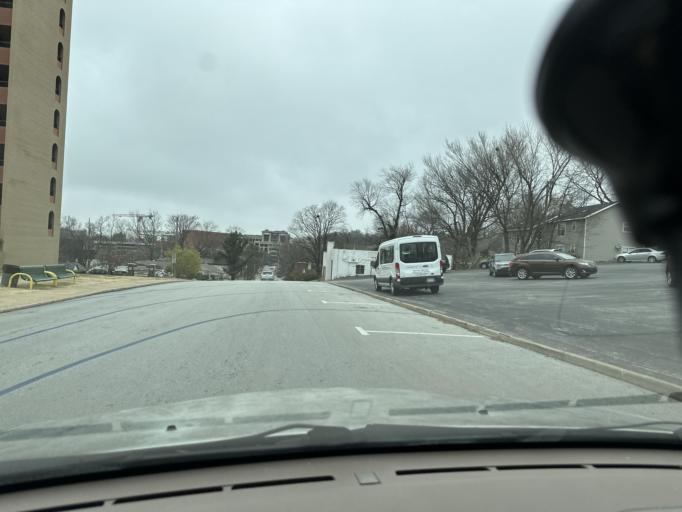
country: US
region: Arkansas
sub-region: Washington County
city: Fayetteville
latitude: 36.0629
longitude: -94.1643
